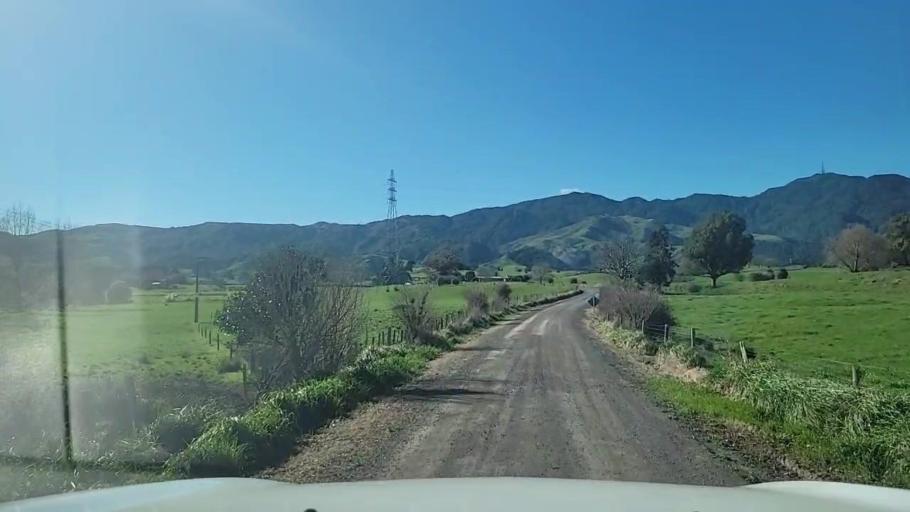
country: NZ
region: Waikato
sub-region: Hauraki District
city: Paeroa
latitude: -37.5005
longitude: 175.6903
